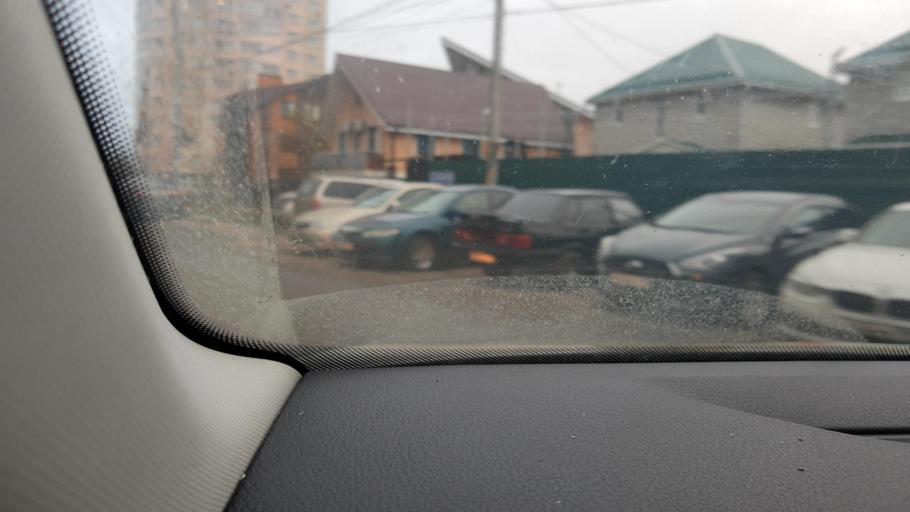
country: RU
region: Moskovskaya
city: Shcherbinka
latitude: 55.5304
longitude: 37.5854
